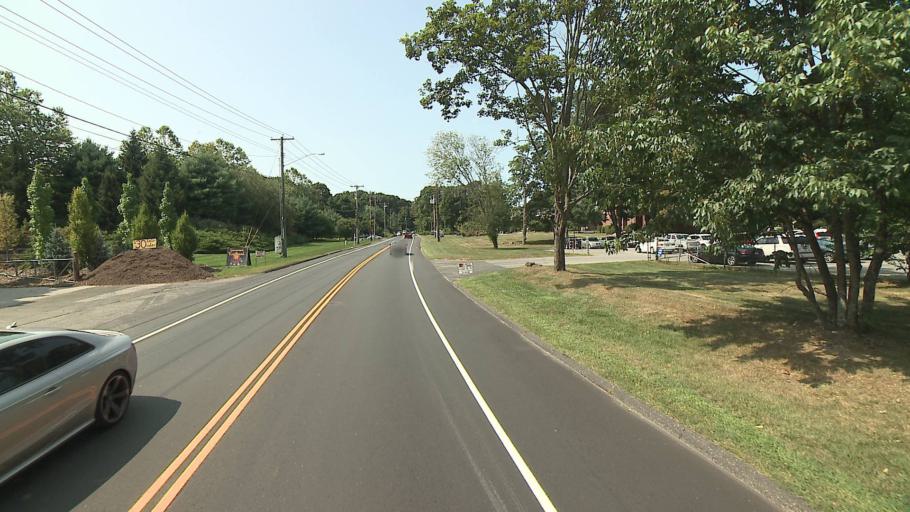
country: US
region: Connecticut
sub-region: Fairfield County
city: Trumbull
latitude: 41.2885
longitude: -73.2389
